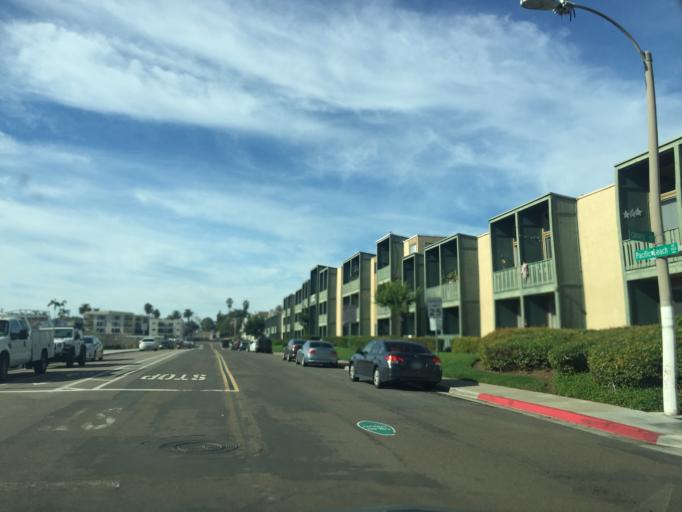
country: US
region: California
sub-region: San Diego County
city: La Jolla
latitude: 32.7966
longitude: -117.2282
